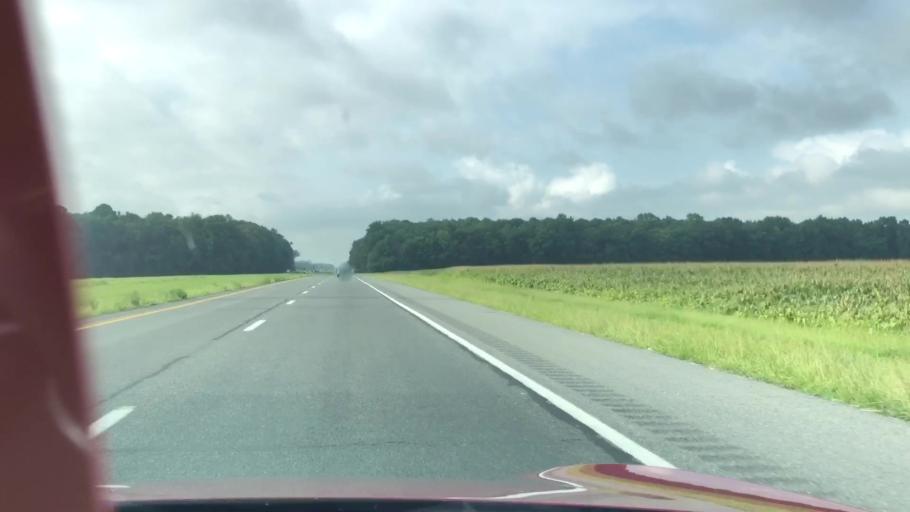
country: US
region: Delaware
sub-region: Sussex County
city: Laurel
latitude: 38.5118
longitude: -75.5573
